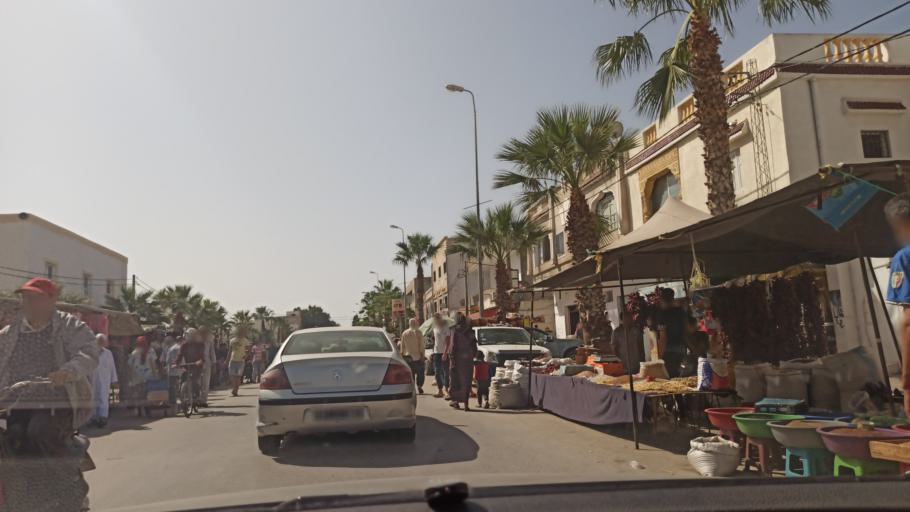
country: TN
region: Manouba
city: Manouba
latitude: 36.7692
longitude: 10.1122
